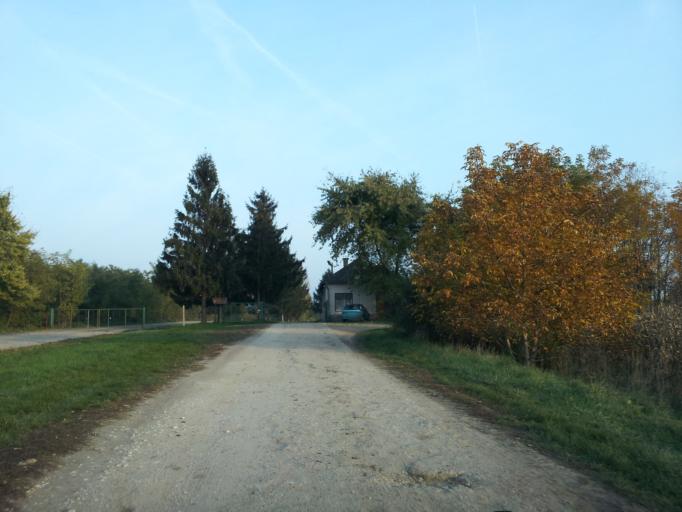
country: HU
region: Komarom-Esztergom
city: Kisber
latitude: 47.4674
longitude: 17.9562
